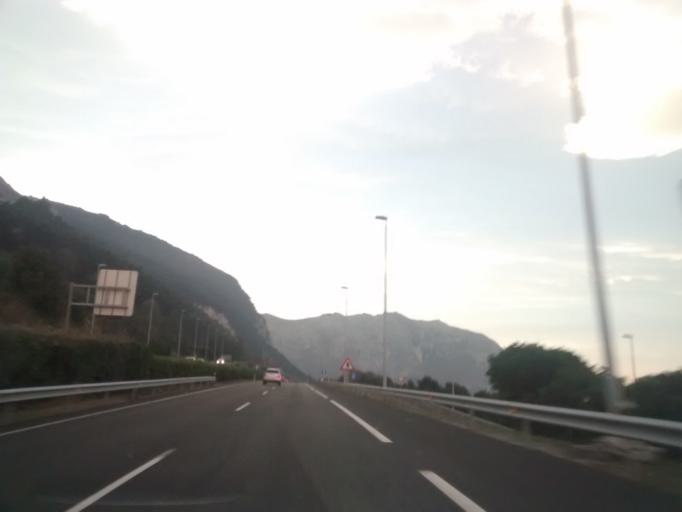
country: ES
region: Cantabria
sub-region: Provincia de Cantabria
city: Liendo
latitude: 43.4026
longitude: -3.2959
